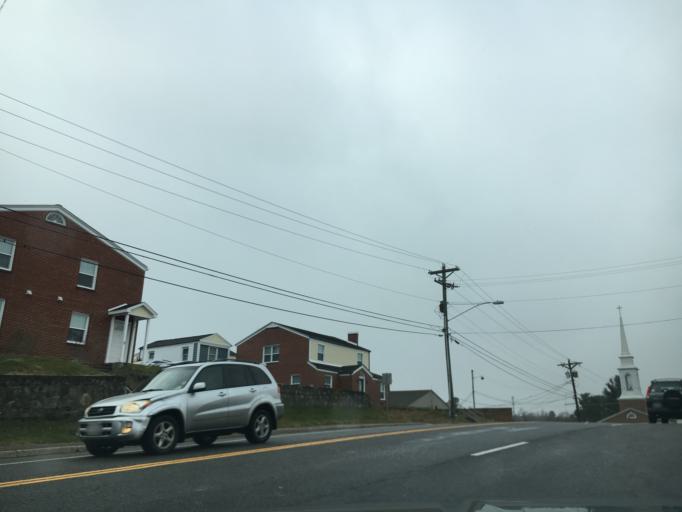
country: US
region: Virginia
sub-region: Montgomery County
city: Christiansburg
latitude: 37.1265
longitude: -80.4111
